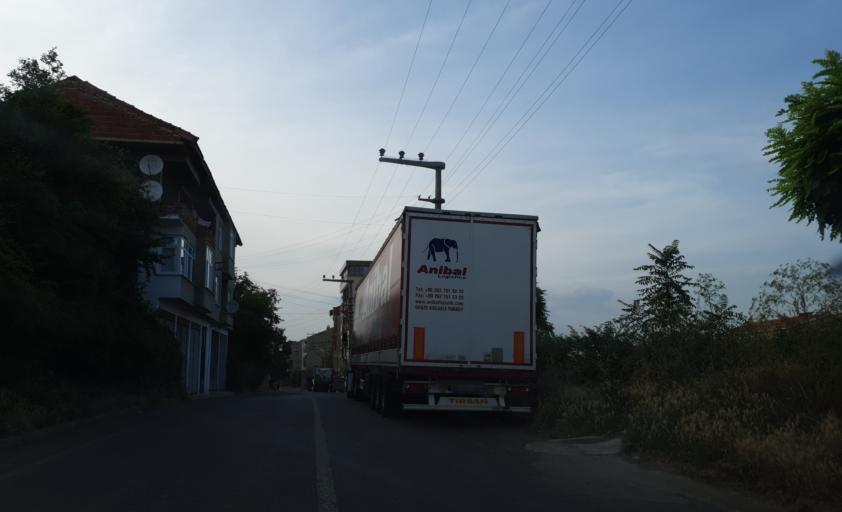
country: TR
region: Tekirdag
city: Hayrabolu
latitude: 41.2138
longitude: 27.1104
